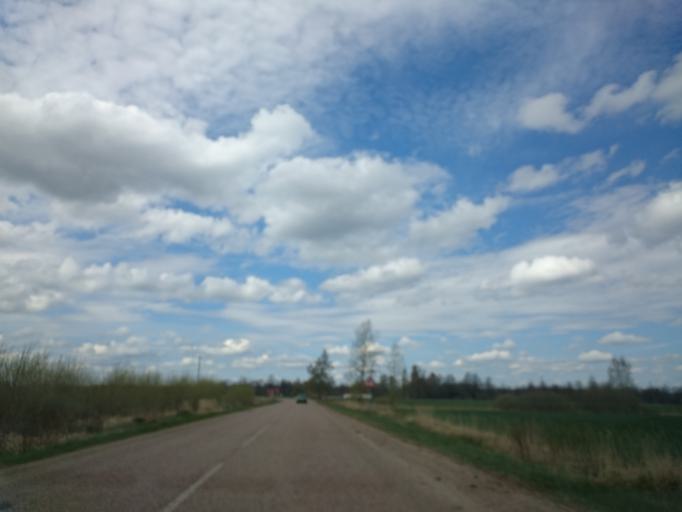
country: LV
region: Talsu Rajons
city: Sabile
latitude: 56.9594
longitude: 22.6233
